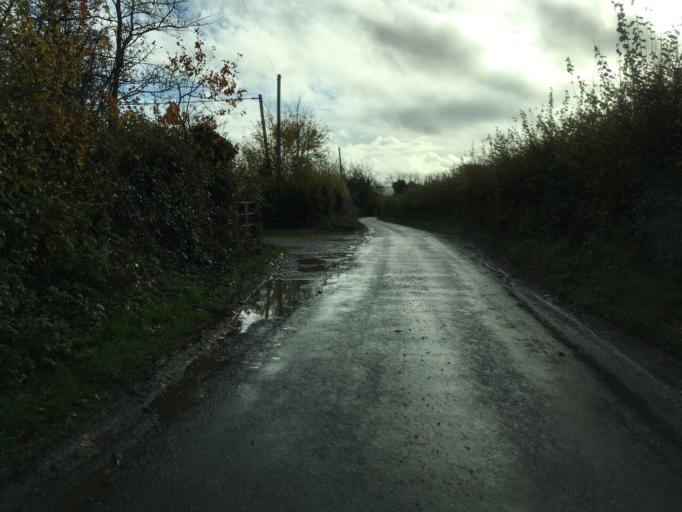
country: GB
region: England
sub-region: South Gloucestershire
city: Pucklechurch
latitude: 51.4746
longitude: -2.4086
